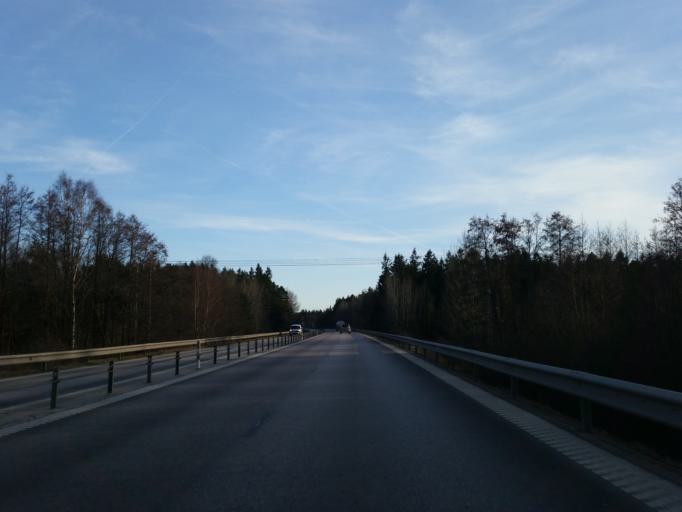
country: SE
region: Kalmar
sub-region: Kalmar Kommun
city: Lindsdal
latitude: 56.7452
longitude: 16.3054
